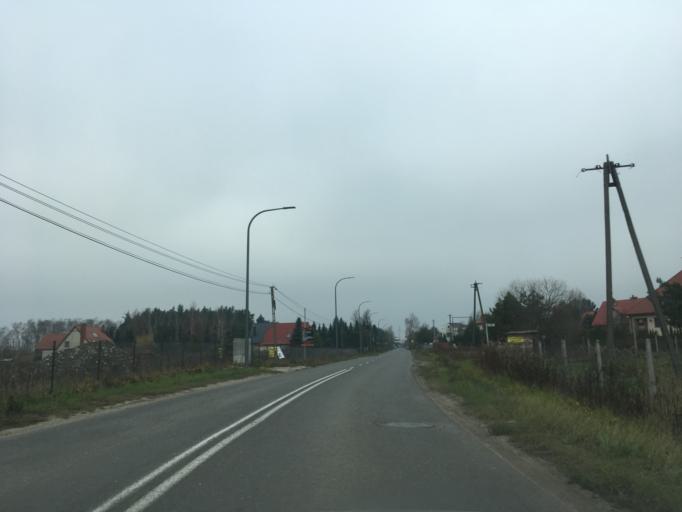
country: PL
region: Masovian Voivodeship
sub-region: Powiat piaseczynski
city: Lesznowola
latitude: 52.0712
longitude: 20.9662
